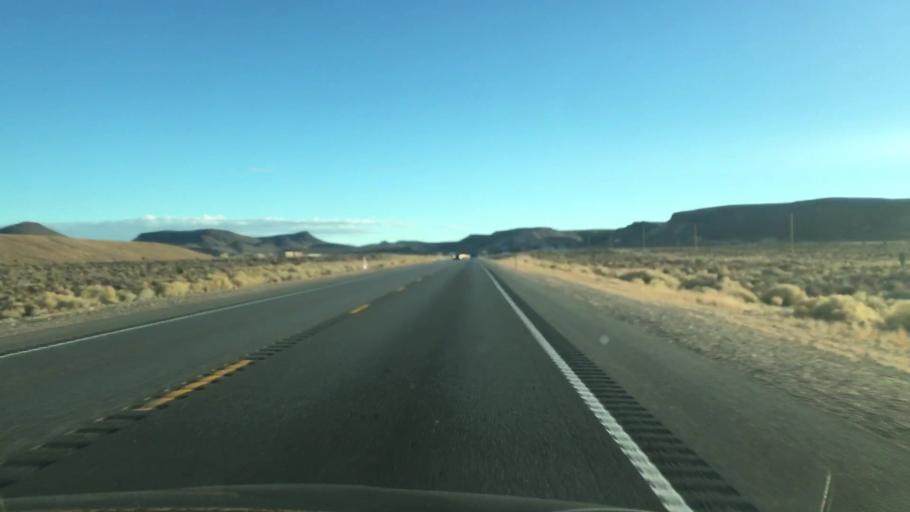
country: US
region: Nevada
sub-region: Esmeralda County
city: Goldfield
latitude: 37.7273
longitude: -117.2442
